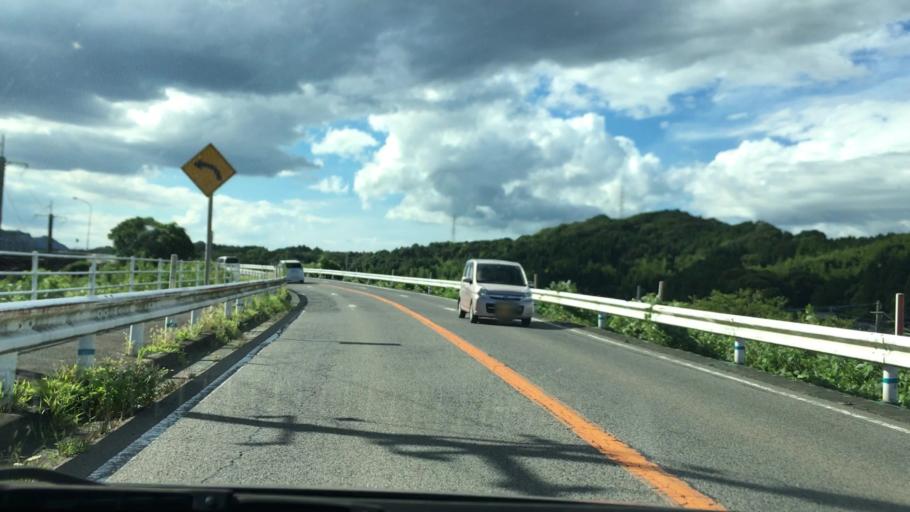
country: JP
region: Saga Prefecture
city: Takeocho-takeo
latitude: 33.1953
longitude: 129.9789
